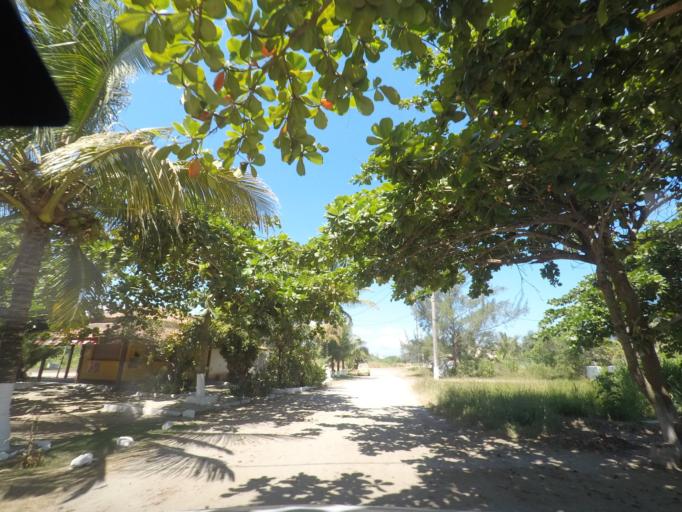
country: BR
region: Rio de Janeiro
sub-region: Marica
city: Marica
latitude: -22.9729
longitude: -42.9216
